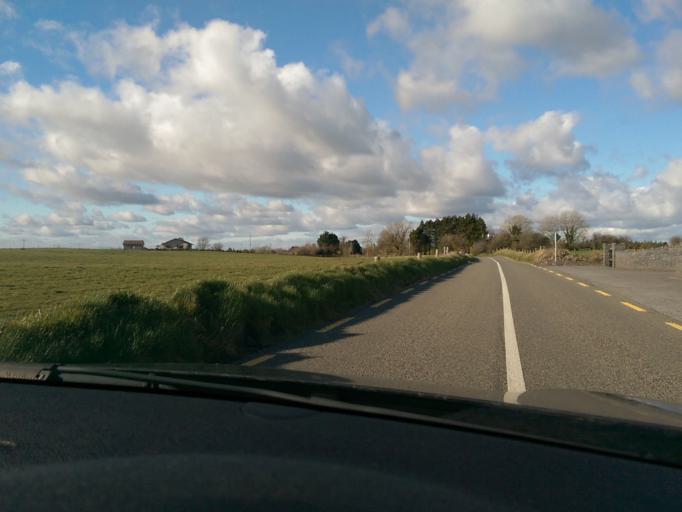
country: IE
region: Connaught
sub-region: Roscommon
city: Castlerea
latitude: 53.5780
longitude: -8.5621
